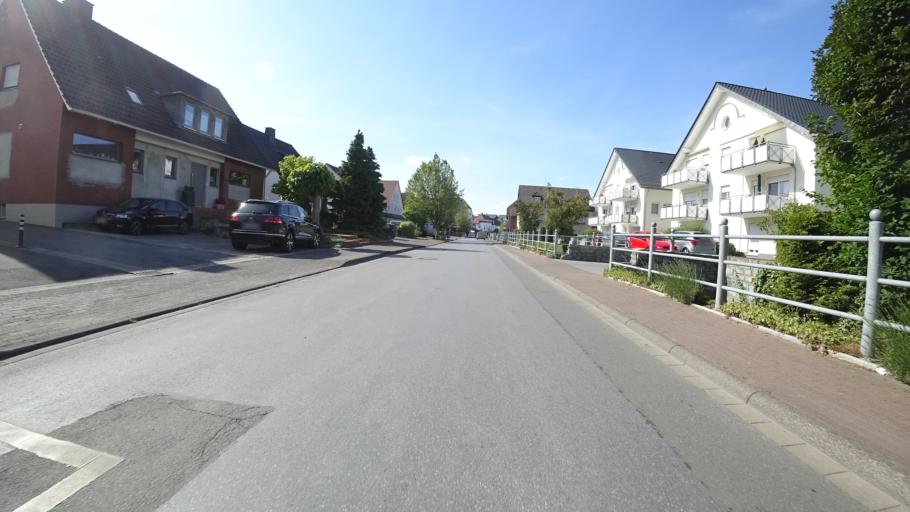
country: DE
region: North Rhine-Westphalia
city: Erwitte
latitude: 51.6307
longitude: 8.3623
